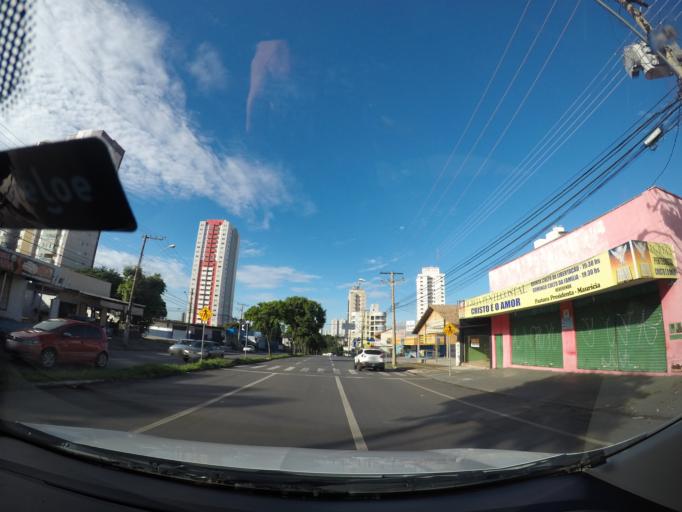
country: BR
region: Goias
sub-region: Goiania
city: Goiania
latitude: -16.7248
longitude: -49.2706
